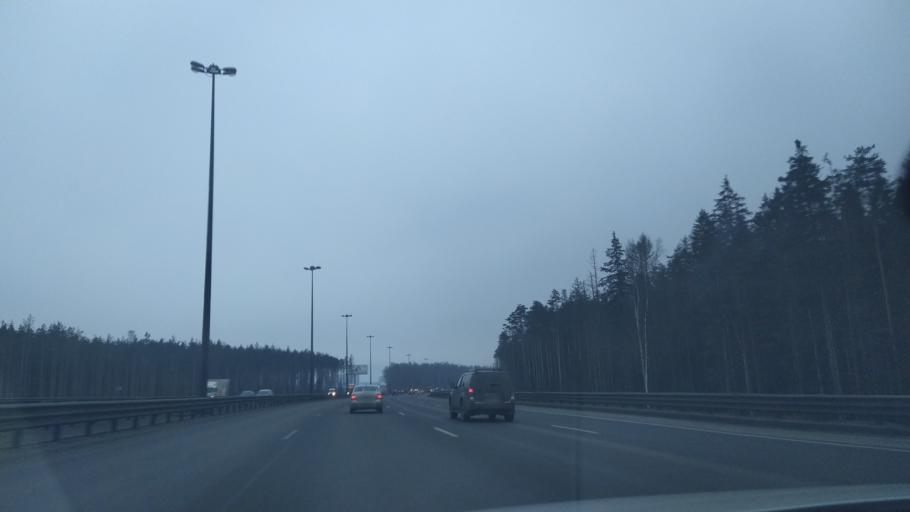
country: RU
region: Leningrad
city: Yanino Vtoroye
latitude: 59.9633
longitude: 30.5538
